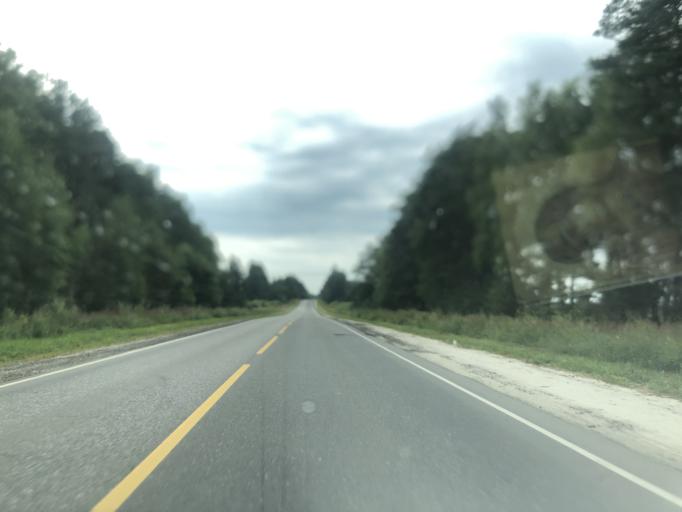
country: RU
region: Ivanovo
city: Pestyaki
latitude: 56.7224
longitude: 42.6273
